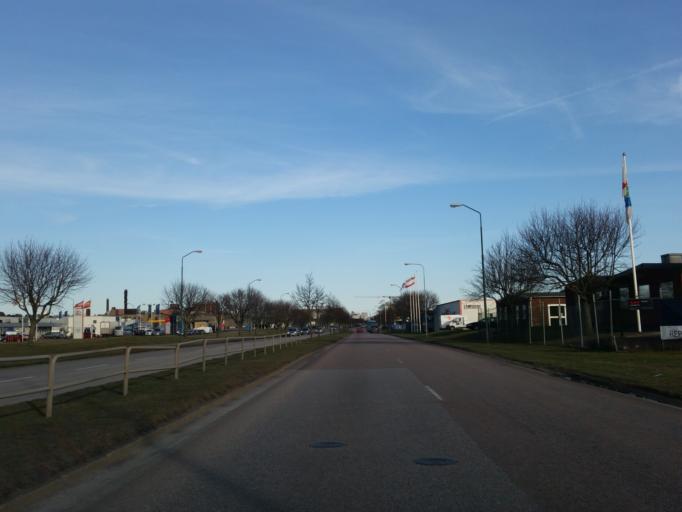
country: SE
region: Kalmar
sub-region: Kalmar Kommun
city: Kalmar
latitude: 56.6730
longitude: 16.3277
